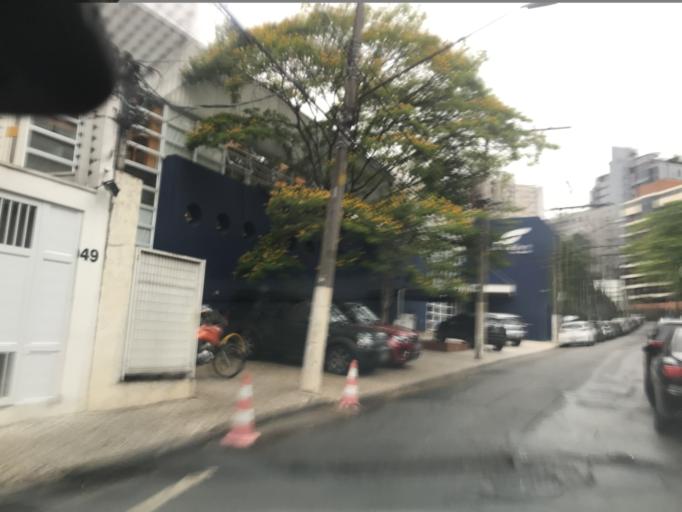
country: BR
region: Sao Paulo
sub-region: Sao Paulo
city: Sao Paulo
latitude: -23.5413
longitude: -46.6788
